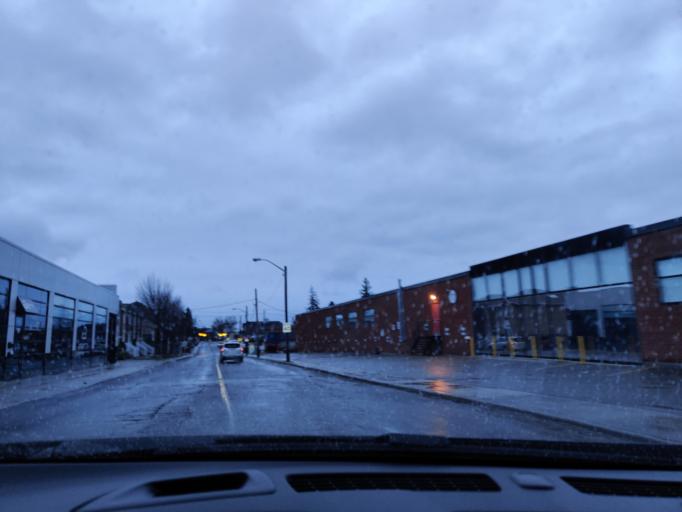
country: CA
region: Ontario
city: Toronto
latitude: 43.6962
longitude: -79.4632
